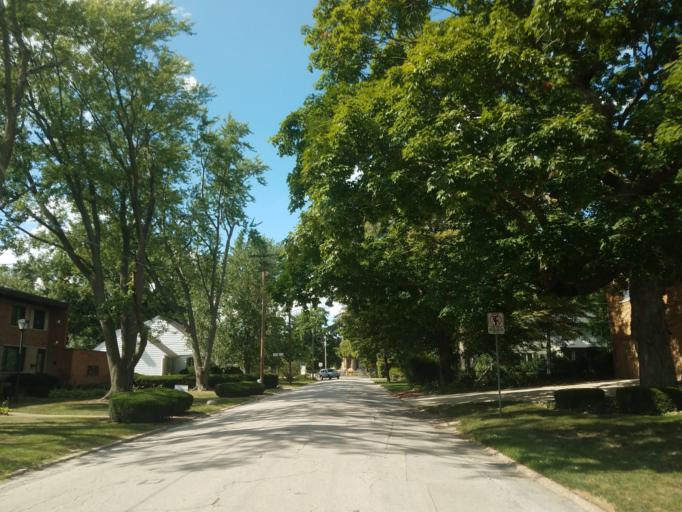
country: US
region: Illinois
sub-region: McLean County
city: Bloomington
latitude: 40.4807
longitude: -88.9807
